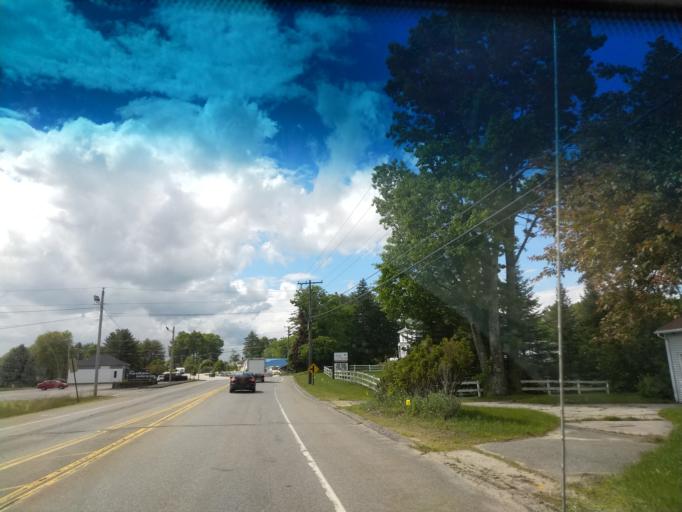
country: US
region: Maine
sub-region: Cumberland County
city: Westbrook
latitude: 43.6850
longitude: -70.3845
